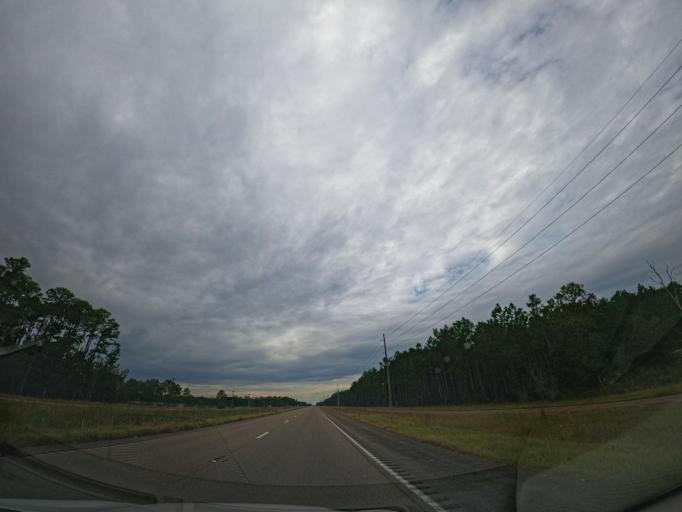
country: US
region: Mississippi
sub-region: Hancock County
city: Waveland
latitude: 30.3006
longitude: -89.4628
